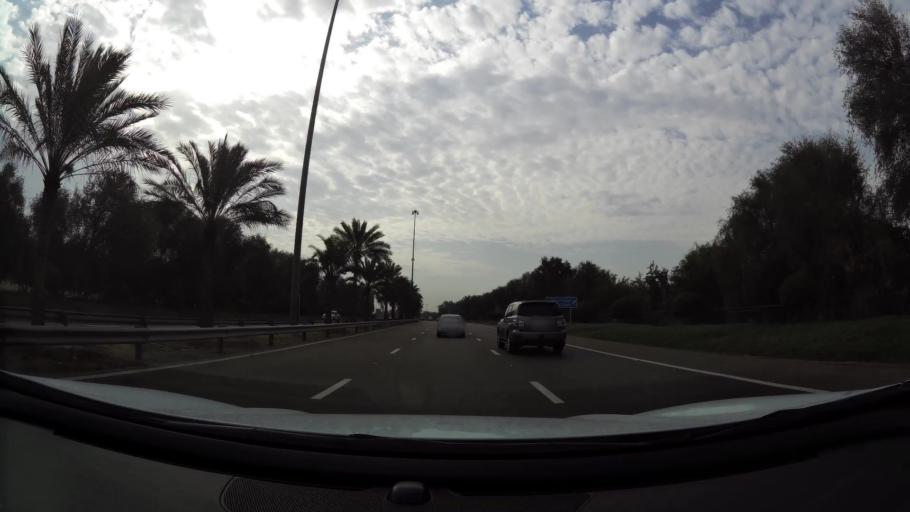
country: AE
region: Abu Dhabi
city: Al Ain
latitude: 24.1912
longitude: 55.5908
